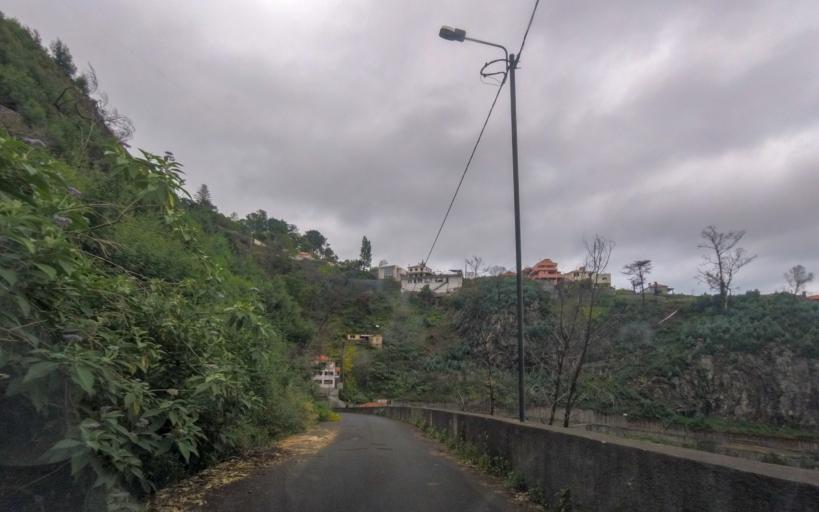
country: PT
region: Madeira
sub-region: Funchal
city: Nossa Senhora do Monte
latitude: 32.6757
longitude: -16.9125
